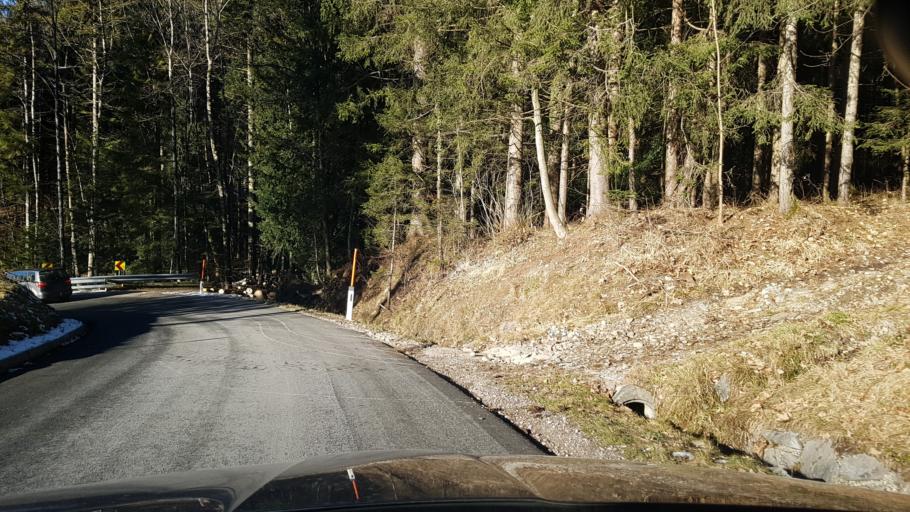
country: AT
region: Salzburg
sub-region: Politischer Bezirk Hallein
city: Golling an der Salzach
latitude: 47.6254
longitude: 13.1883
